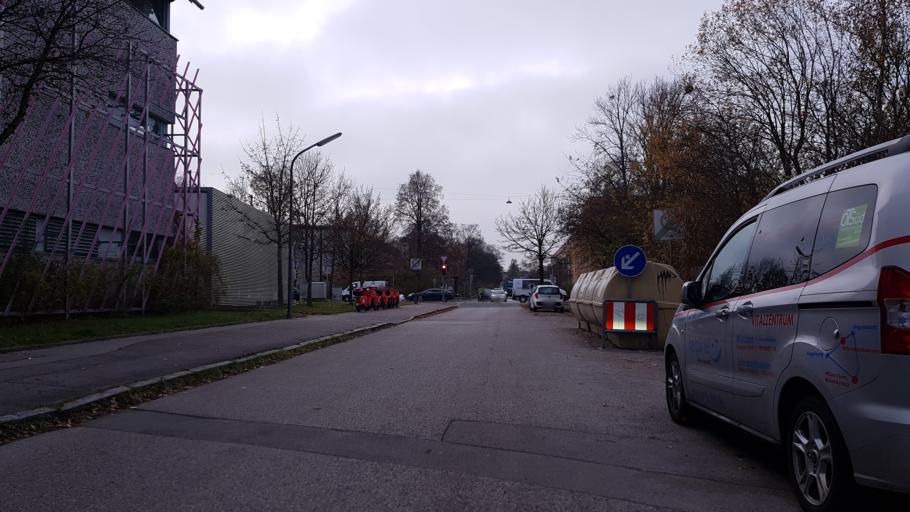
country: DE
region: Bavaria
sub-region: Upper Bavaria
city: Munich
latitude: 48.1097
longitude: 11.6072
